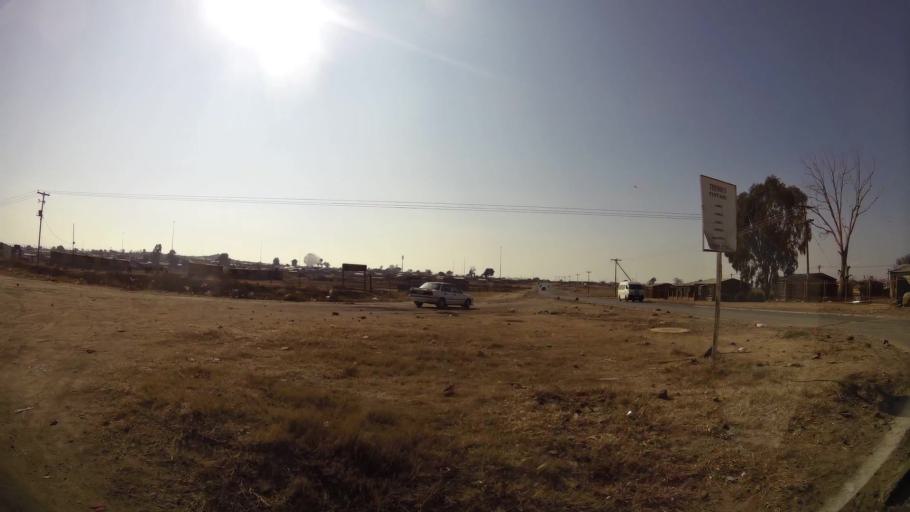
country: ZA
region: Orange Free State
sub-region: Mangaung Metropolitan Municipality
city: Bloemfontein
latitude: -29.1976
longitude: 26.2618
